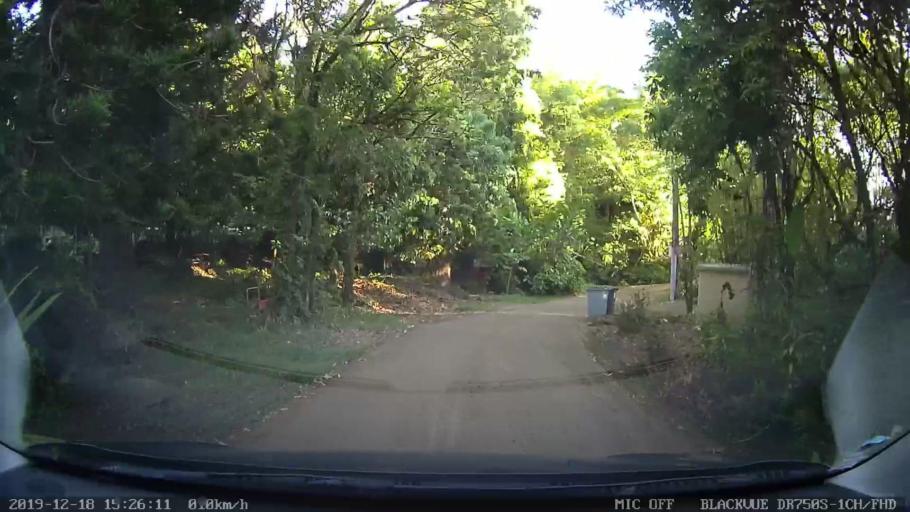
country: RE
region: Reunion
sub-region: Reunion
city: Bras-Panon
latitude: -21.0024
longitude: 55.6521
